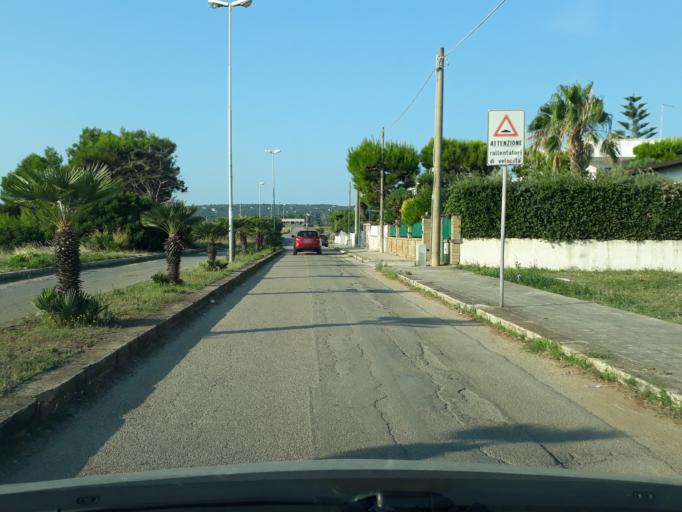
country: IT
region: Apulia
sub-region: Provincia di Brindisi
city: Carovigno
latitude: 40.7560
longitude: 17.6946
